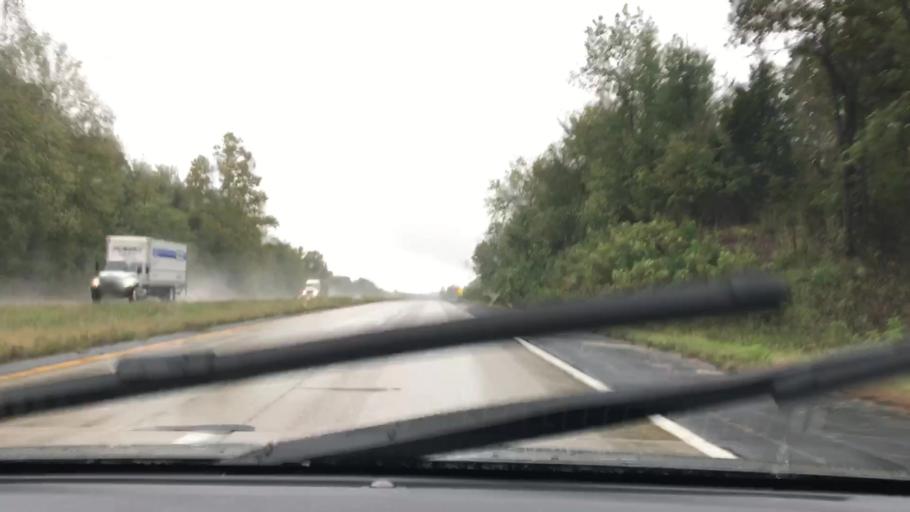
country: US
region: Kentucky
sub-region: Hopkins County
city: Nortonville
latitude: 37.1422
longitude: -87.4635
